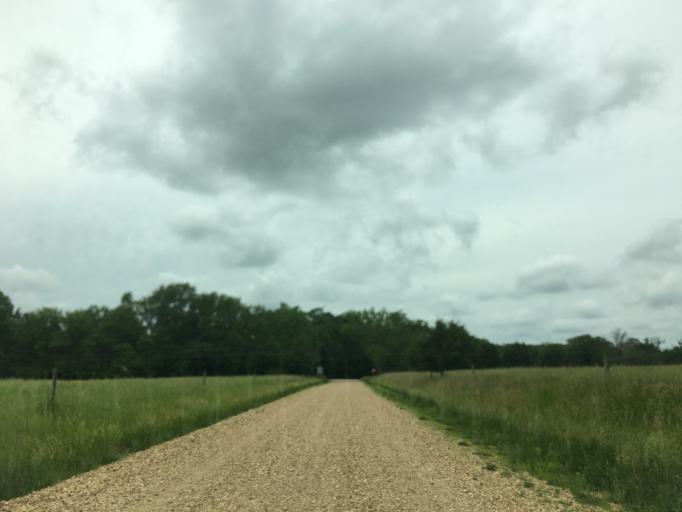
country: US
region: Missouri
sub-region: Gasconade County
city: Owensville
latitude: 38.4504
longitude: -91.4462
